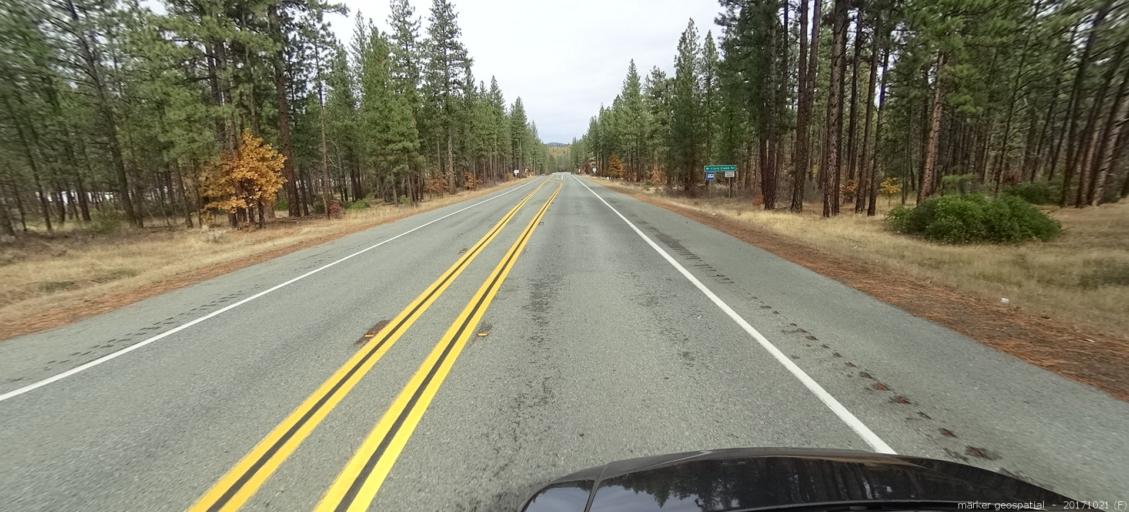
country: US
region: California
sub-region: Shasta County
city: Burney
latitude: 40.9948
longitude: -121.6286
